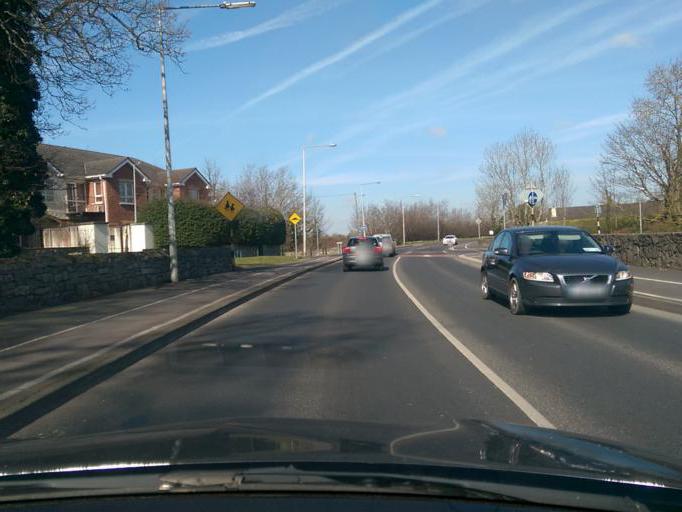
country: IE
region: Leinster
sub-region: Kildare
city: Celbridge
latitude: 53.3523
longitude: -6.5468
